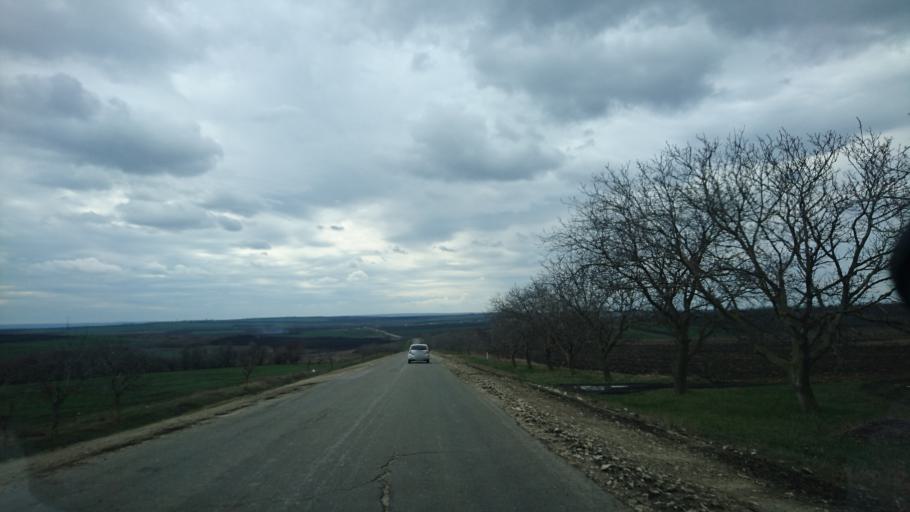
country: MD
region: Gagauzia
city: Comrat
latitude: 46.3088
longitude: 28.6041
